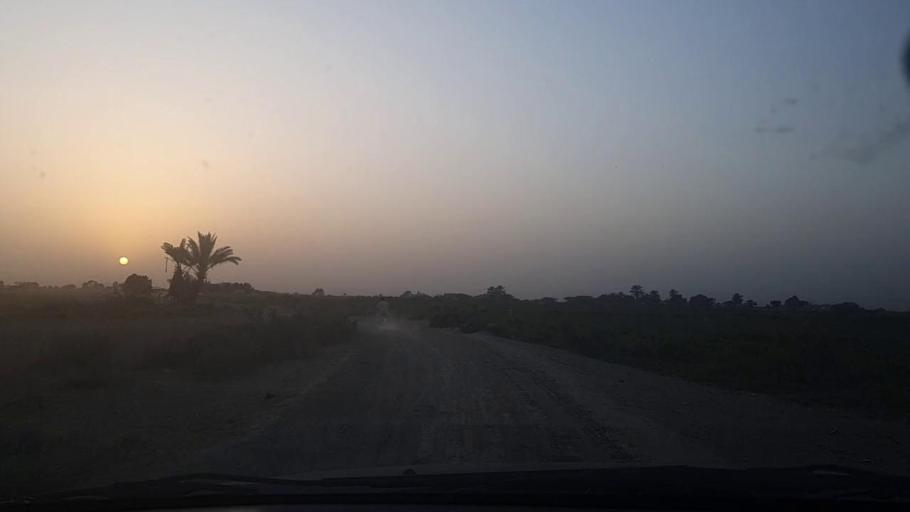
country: PK
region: Sindh
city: Mirpur Sakro
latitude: 24.3793
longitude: 67.6530
